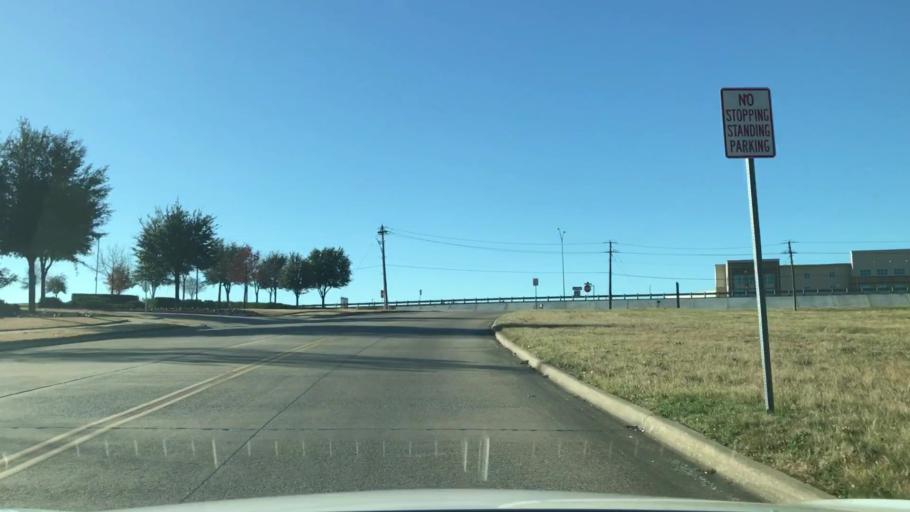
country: US
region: Texas
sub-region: Dallas County
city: Coppell
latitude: 32.9011
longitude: -96.9791
